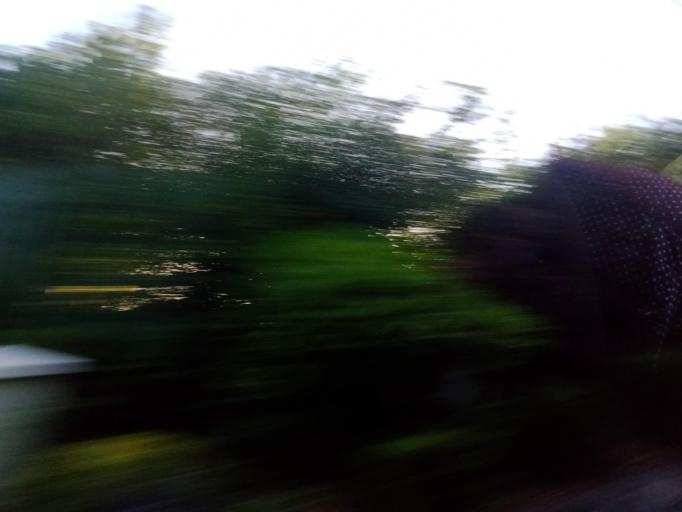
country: IE
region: Leinster
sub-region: Kilkenny
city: Castlecomer
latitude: 52.7457
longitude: -7.2356
